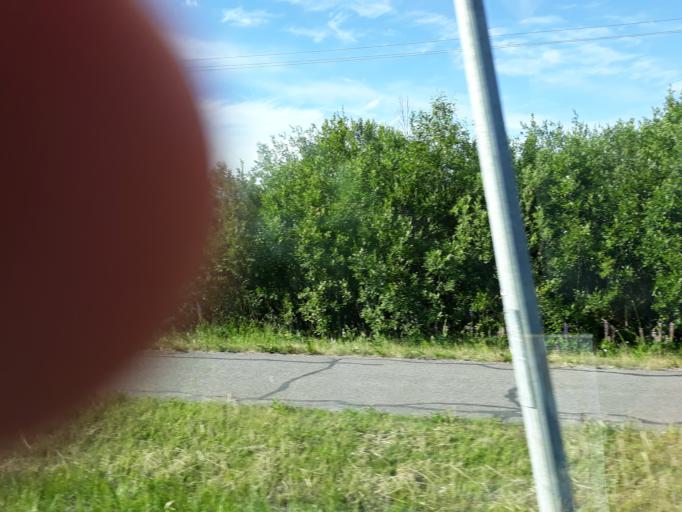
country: FI
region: Uusimaa
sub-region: Helsinki
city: Jaervenpaeae
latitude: 60.5413
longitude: 24.9933
